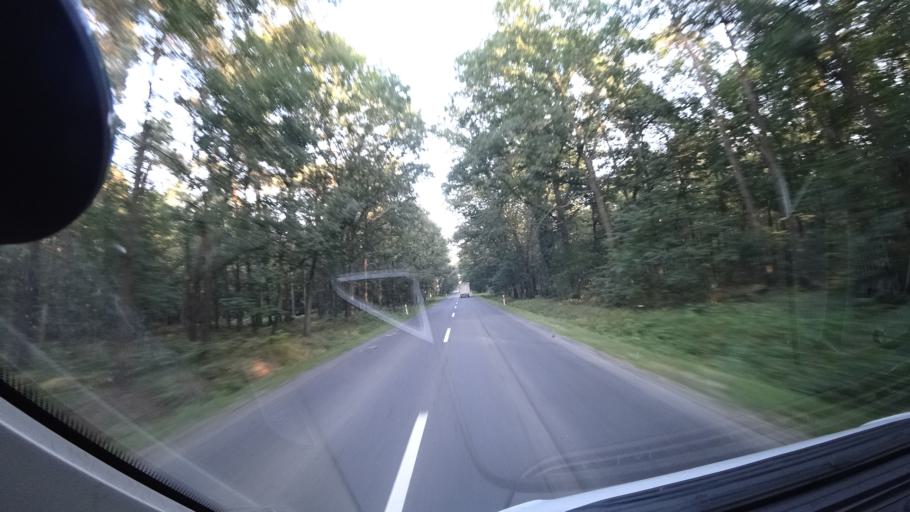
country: PL
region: Silesian Voivodeship
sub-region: Powiat gliwicki
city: Rudziniec
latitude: 50.2740
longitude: 18.3885
